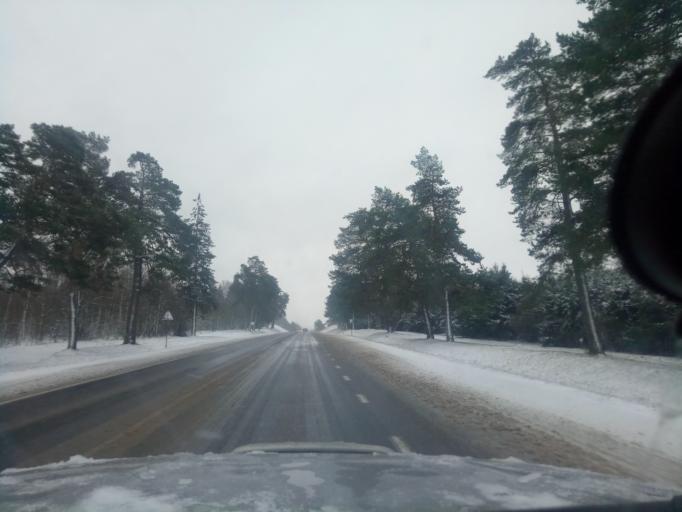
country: BY
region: Minsk
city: Haradzyeya
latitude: 53.2703
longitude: 26.6007
